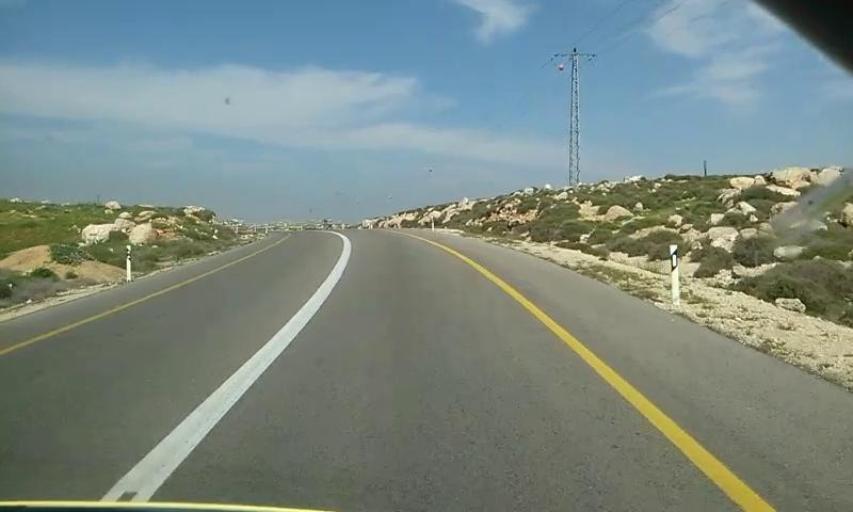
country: PS
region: West Bank
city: As Samu`
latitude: 31.3967
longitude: 35.0281
